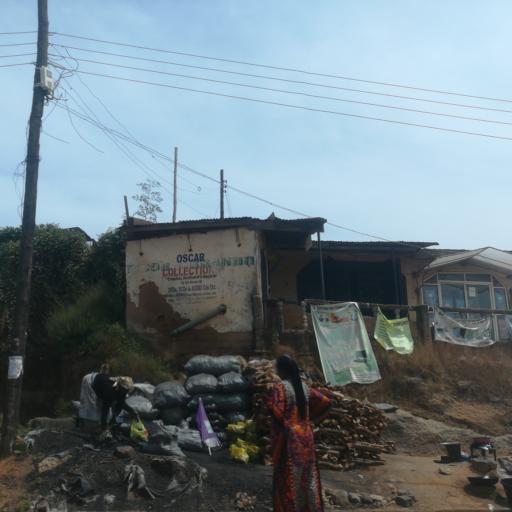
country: NG
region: Plateau
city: Jos
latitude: 9.8929
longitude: 8.8645
